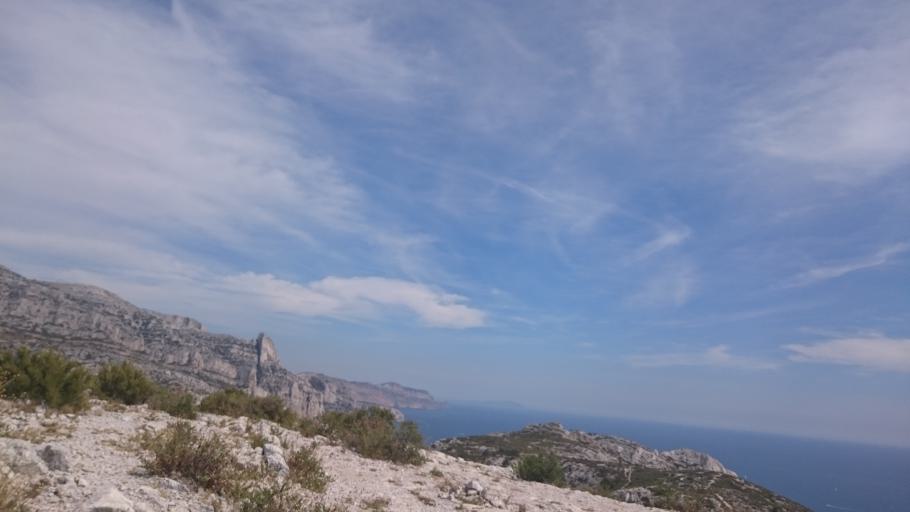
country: FR
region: Provence-Alpes-Cote d'Azur
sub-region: Departement des Bouches-du-Rhone
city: Marseille 09
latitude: 43.2159
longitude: 5.4269
